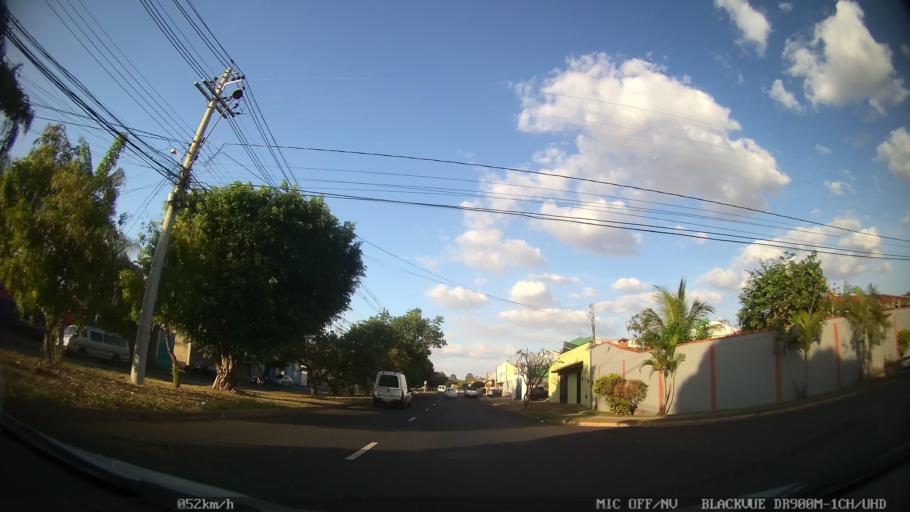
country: BR
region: Sao Paulo
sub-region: Ribeirao Preto
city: Ribeirao Preto
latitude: -21.1678
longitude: -47.7519
